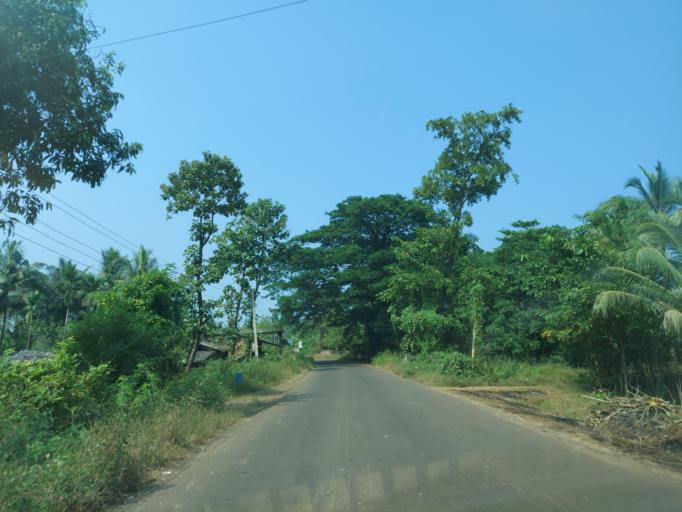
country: IN
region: Maharashtra
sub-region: Sindhudurg
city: Kudal
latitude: 15.9885
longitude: 73.6795
